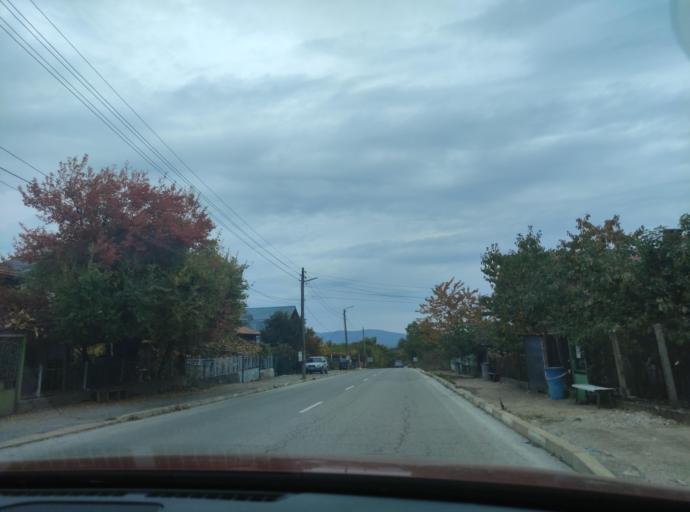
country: BG
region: Montana
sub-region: Obshtina Berkovitsa
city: Berkovitsa
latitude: 43.2080
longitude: 23.1598
